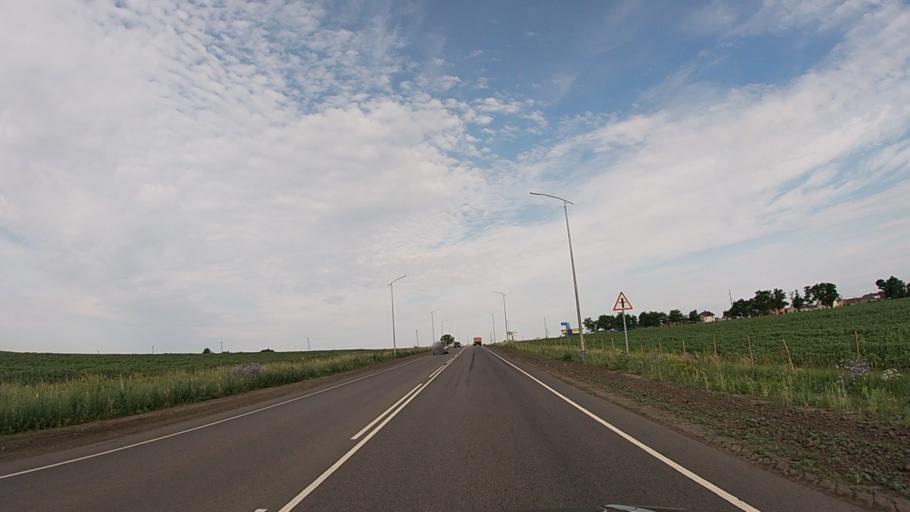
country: RU
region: Belgorod
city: Severnyy
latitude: 50.6650
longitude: 36.5060
